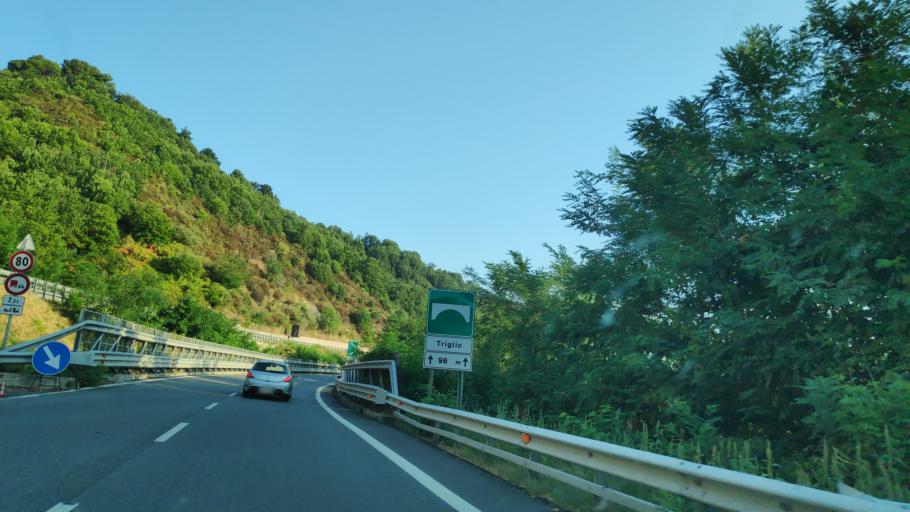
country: IT
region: Calabria
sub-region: Provincia di Cosenza
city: Belsito
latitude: 39.1578
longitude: 16.2877
